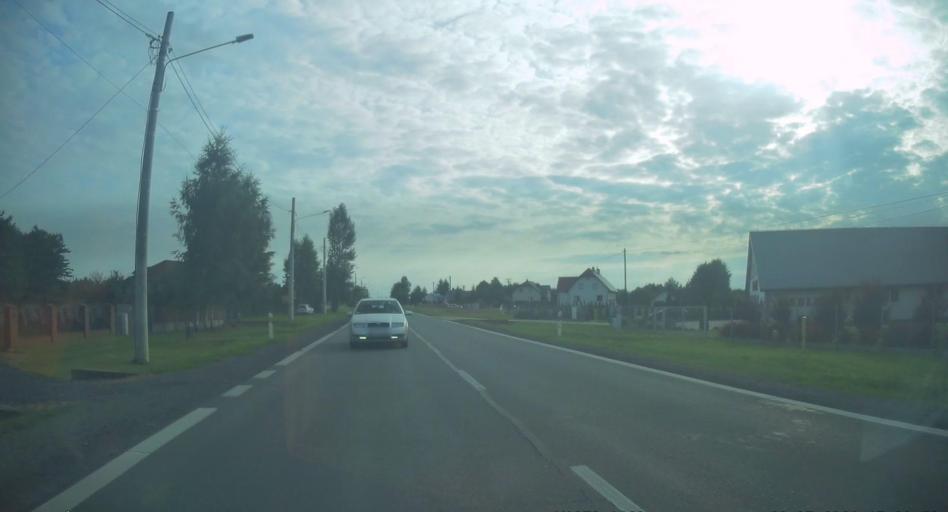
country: PL
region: Silesian Voivodeship
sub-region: Powiat czestochowski
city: Rudniki
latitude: 50.8859
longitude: 19.2596
